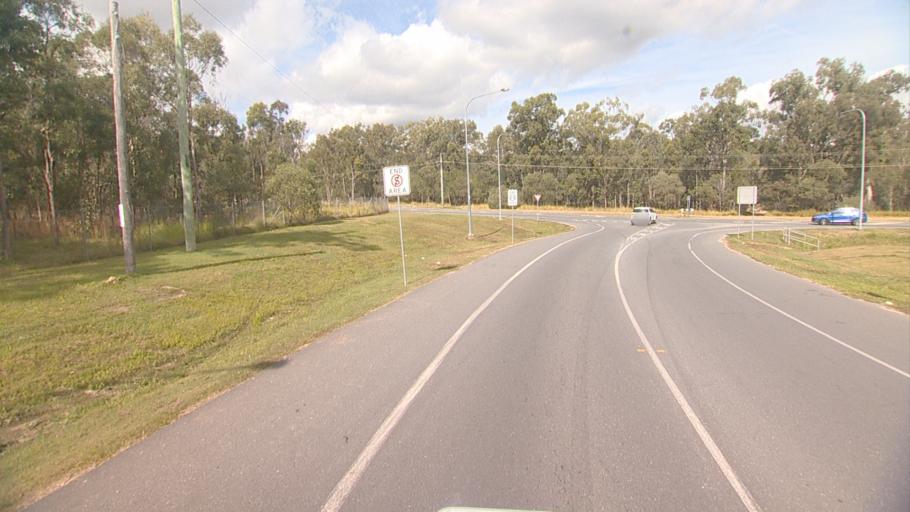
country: AU
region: Queensland
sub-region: Logan
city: Logan Reserve
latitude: -27.6923
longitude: 153.0705
